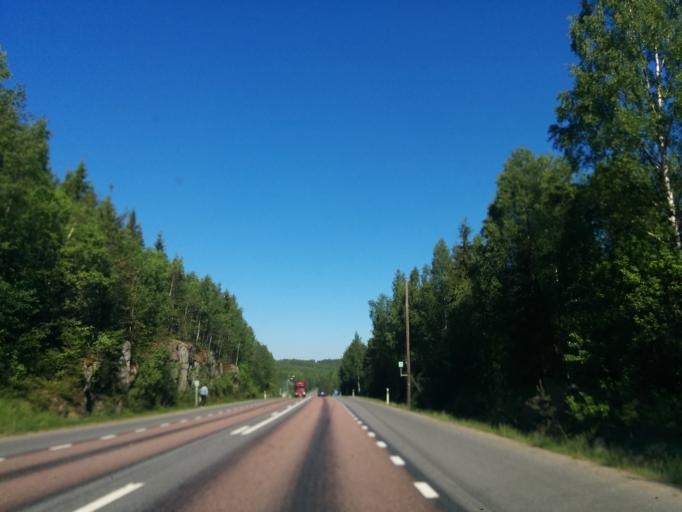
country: SE
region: Vaesternorrland
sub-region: Kramfors Kommun
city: Kramfors
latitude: 62.9592
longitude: 17.7518
